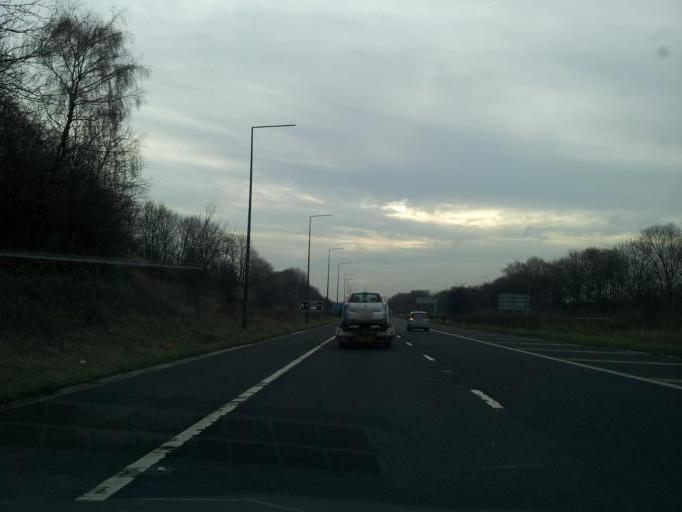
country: GB
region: England
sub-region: Borough of Rochdale
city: Rochdale
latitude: 53.5830
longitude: -2.1576
